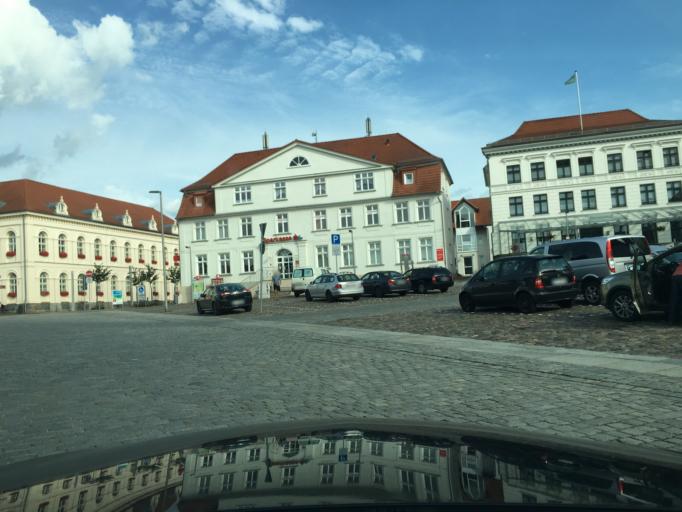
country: DE
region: Mecklenburg-Vorpommern
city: Neustrelitz
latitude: 53.3628
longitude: 13.0619
